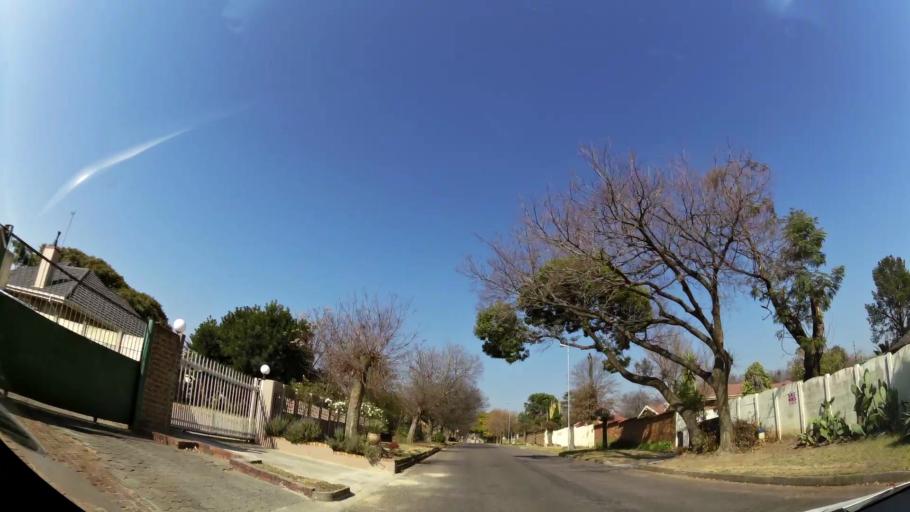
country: ZA
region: Gauteng
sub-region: Ekurhuleni Metropolitan Municipality
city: Boksburg
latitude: -26.2431
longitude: 28.2510
